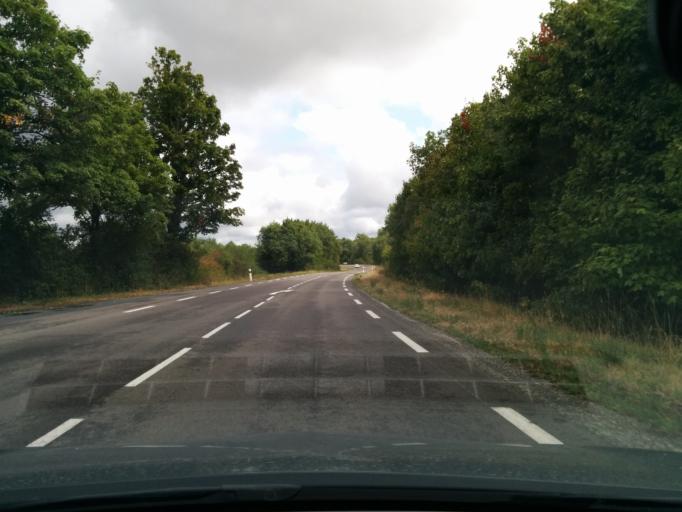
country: FR
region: Midi-Pyrenees
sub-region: Departement du Lot
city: Souillac
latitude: 44.9502
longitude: 1.4958
